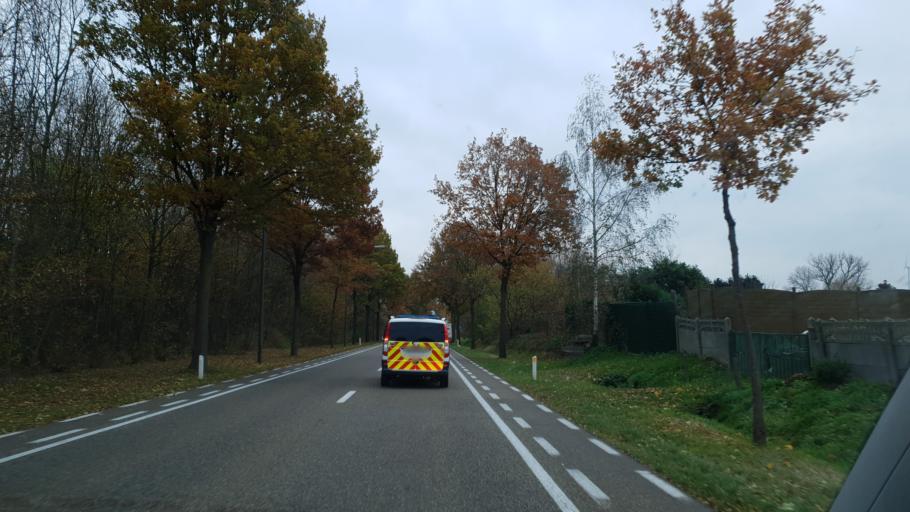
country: BE
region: Flanders
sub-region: Provincie Limburg
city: Lanaken
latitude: 50.8950
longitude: 5.6505
